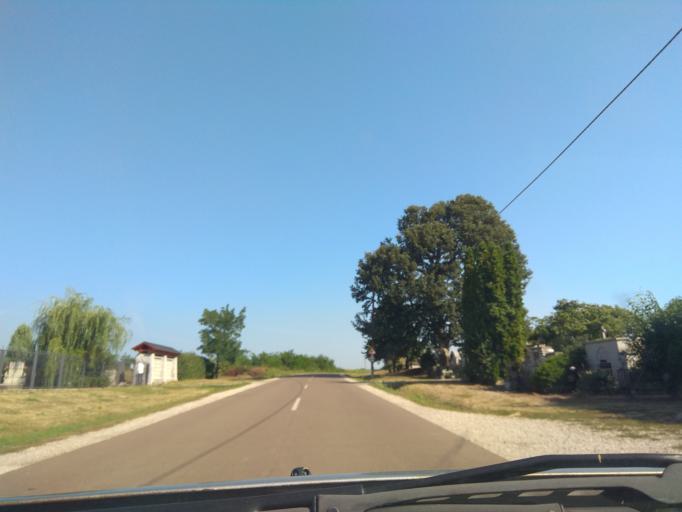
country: HU
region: Borsod-Abauj-Zemplen
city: Emod
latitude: 47.9507
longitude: 20.8100
